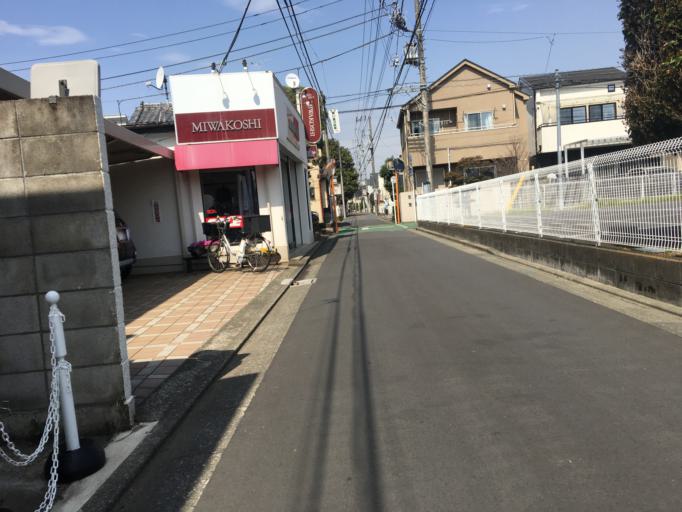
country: JP
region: Tokyo
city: Kamirenjaku
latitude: 35.6929
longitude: 139.5428
